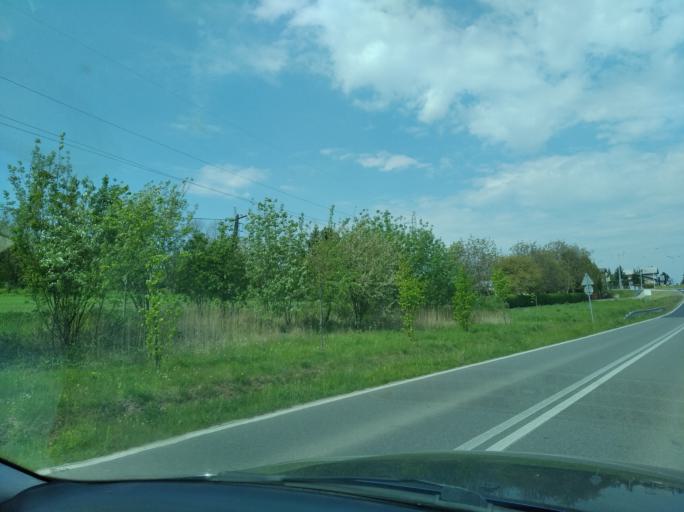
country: PL
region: Subcarpathian Voivodeship
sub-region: Powiat jaroslawski
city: Jaroslaw
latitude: 49.9997
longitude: 22.6740
